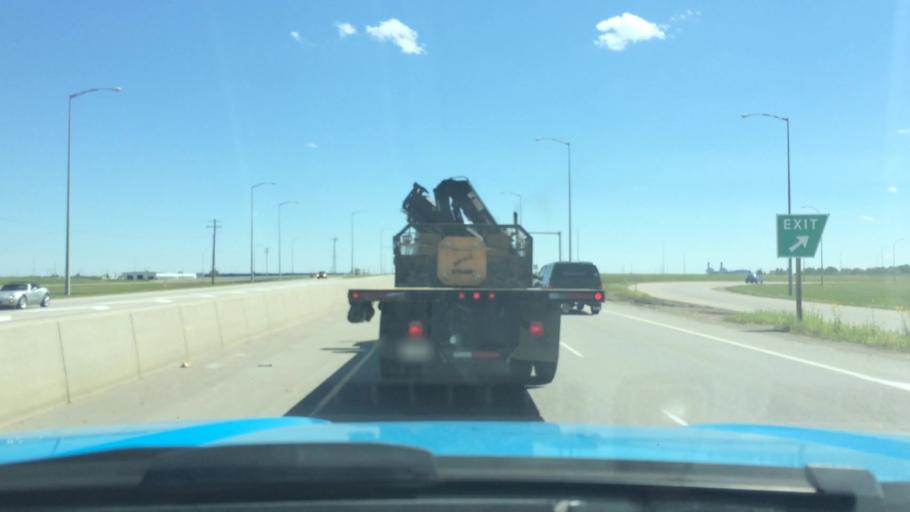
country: CA
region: Alberta
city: Chestermere
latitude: 50.9795
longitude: -113.9281
